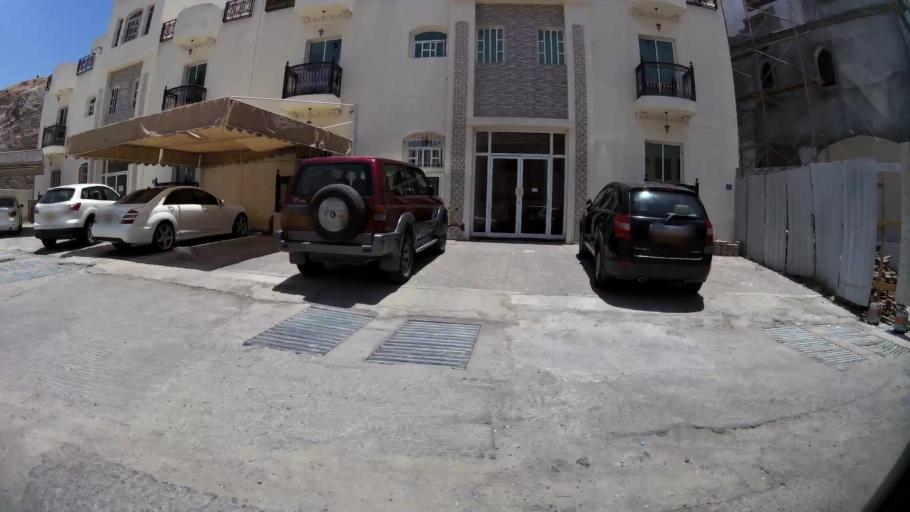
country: OM
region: Muhafazat Masqat
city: Muscat
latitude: 23.6144
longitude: 58.5422
